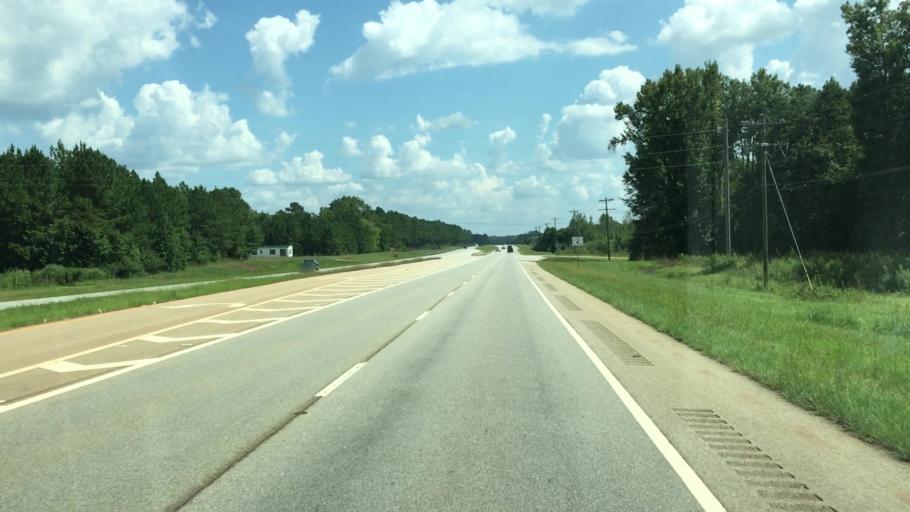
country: US
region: Georgia
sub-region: Putnam County
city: Eatonton
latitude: 33.2605
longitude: -83.3324
